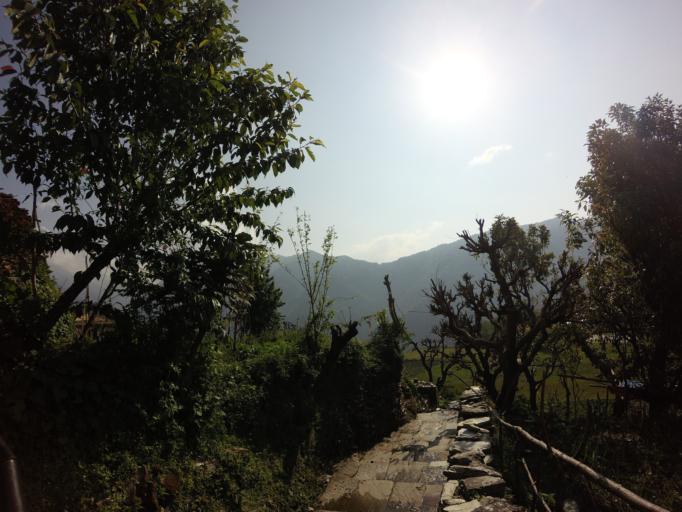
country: NP
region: Western Region
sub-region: Dhawalagiri Zone
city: Chitre
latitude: 28.3768
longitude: 83.8097
